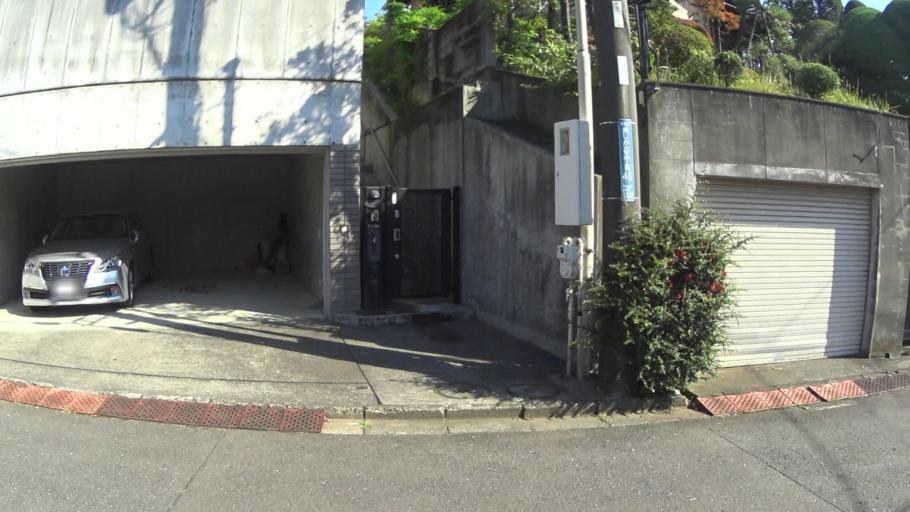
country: JP
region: Tokyo
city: Chofugaoka
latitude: 35.5860
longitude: 139.5502
